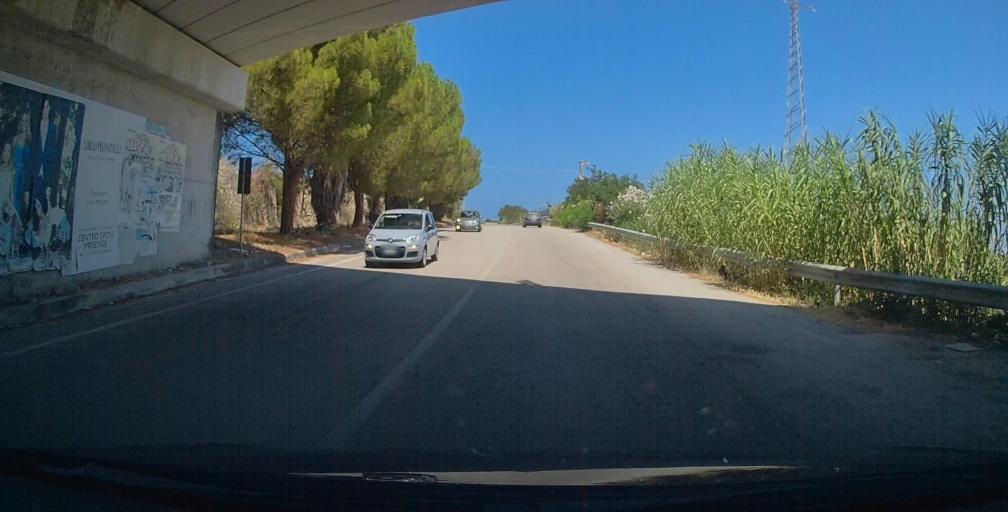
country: IT
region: Sicily
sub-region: Messina
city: Patti
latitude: 38.1400
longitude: 14.9970
